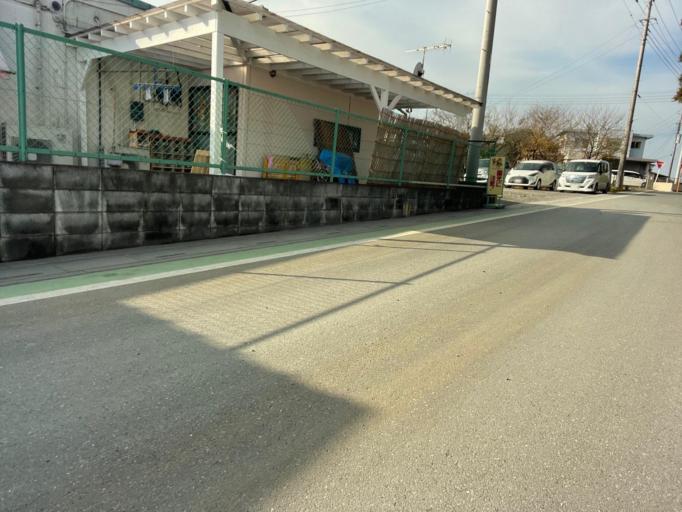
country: JP
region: Saitama
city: Yorii
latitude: 36.1608
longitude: 139.1780
